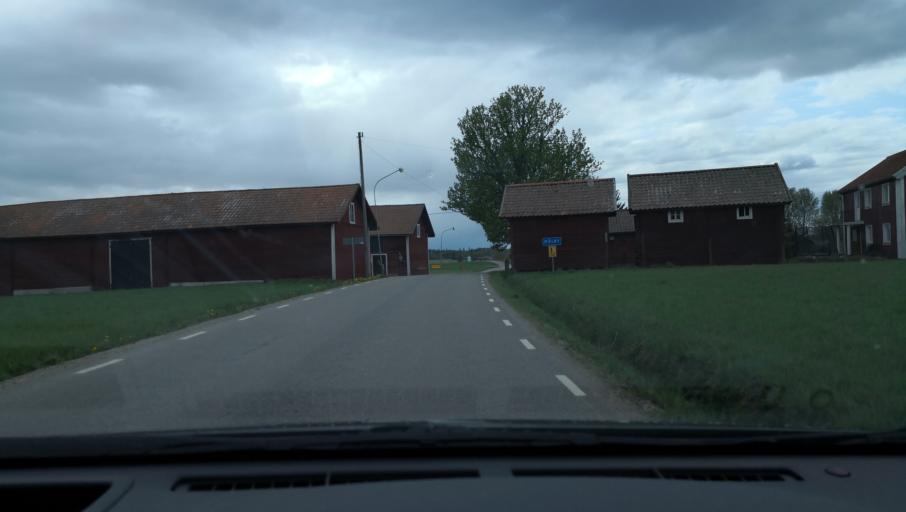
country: SE
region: Dalarna
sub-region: Avesta Kommun
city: Avesta
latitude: 60.0208
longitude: 16.3012
